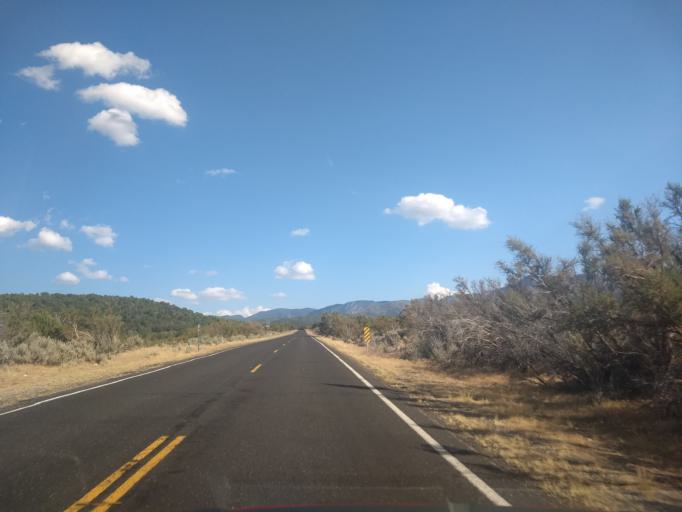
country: US
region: Utah
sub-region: Washington County
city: Enterprise
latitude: 37.4207
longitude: -113.5754
